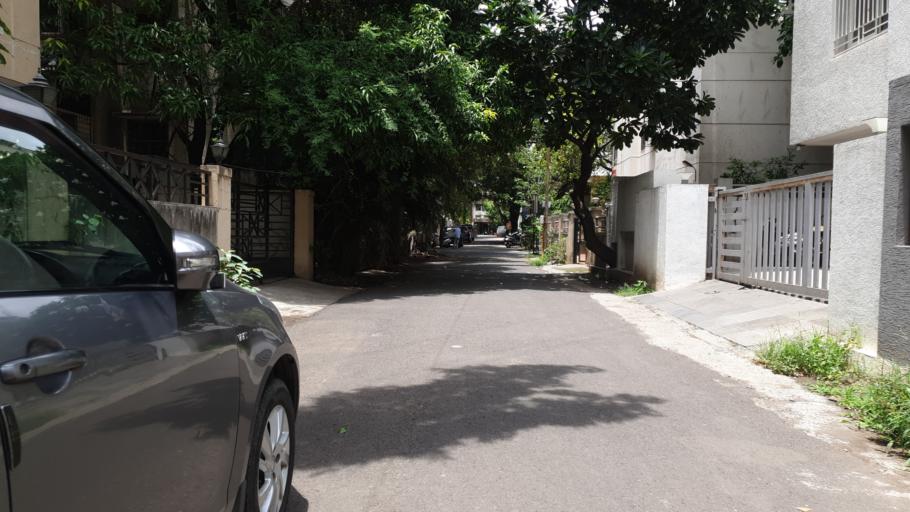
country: IN
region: Maharashtra
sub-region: Pune Division
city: Pune
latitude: 18.4923
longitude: 73.8270
